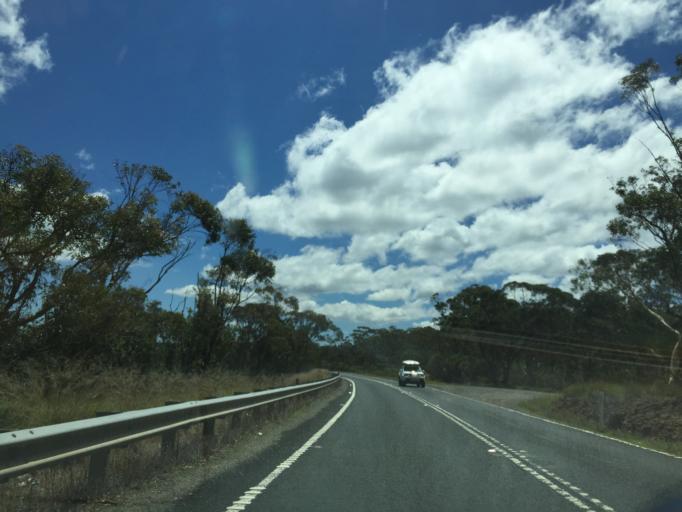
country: AU
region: New South Wales
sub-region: Blue Mountains Municipality
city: Blackheath
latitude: -33.5689
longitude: 150.3499
